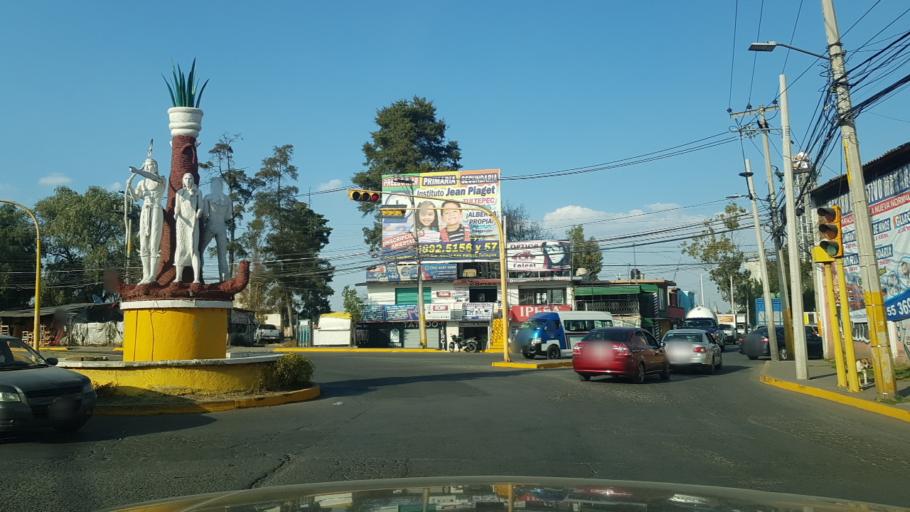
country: MX
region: Mexico
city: Santiago Teyahualco
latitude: 19.6613
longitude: -99.1274
